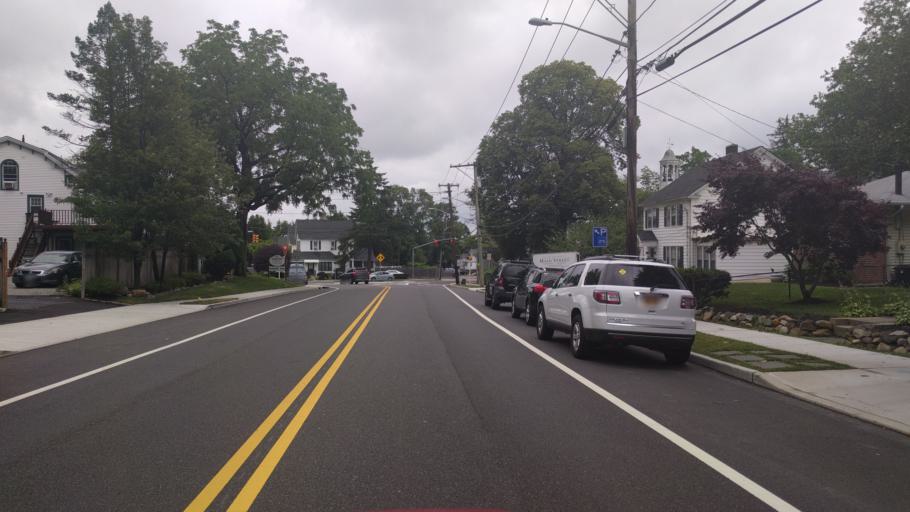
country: US
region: New York
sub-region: Suffolk County
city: Huntington
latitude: 40.8666
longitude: -73.4277
